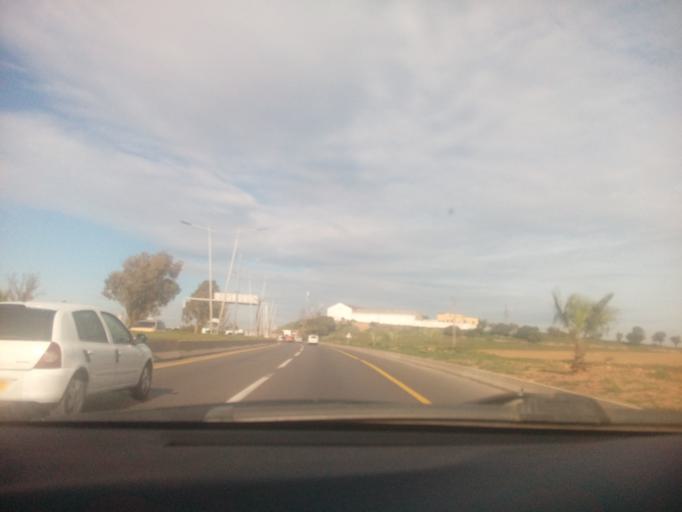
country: DZ
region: Oran
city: Es Senia
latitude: 35.6705
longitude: -0.5951
